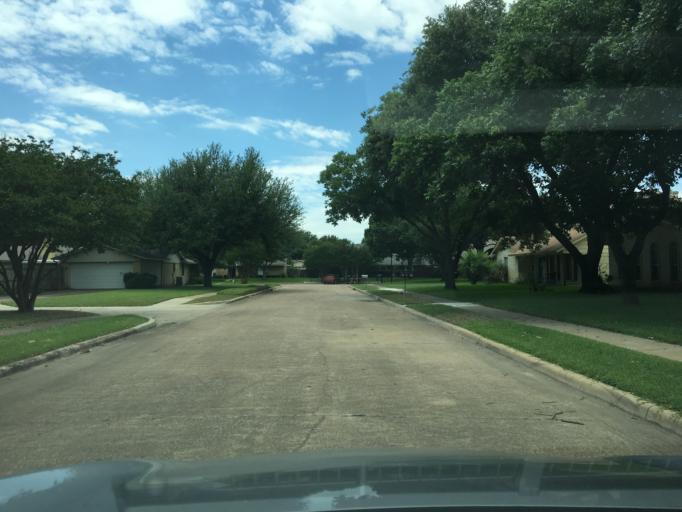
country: US
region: Texas
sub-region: Dallas County
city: Richardson
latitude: 32.9375
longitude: -96.6874
